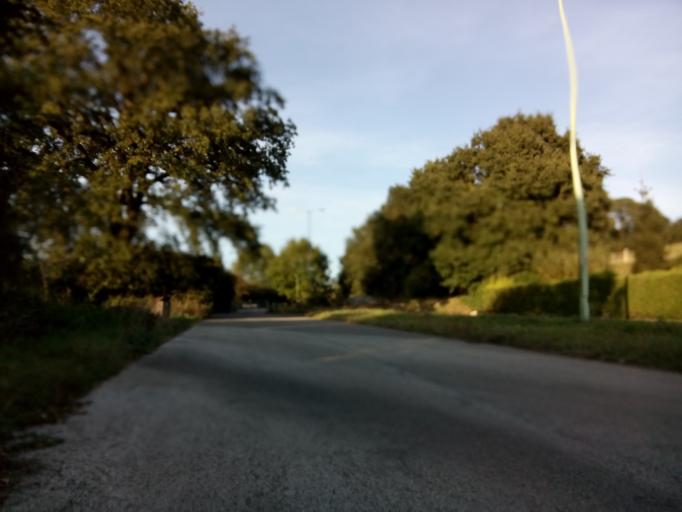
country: GB
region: England
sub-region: Suffolk
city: Bramford
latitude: 52.0388
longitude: 1.0925
